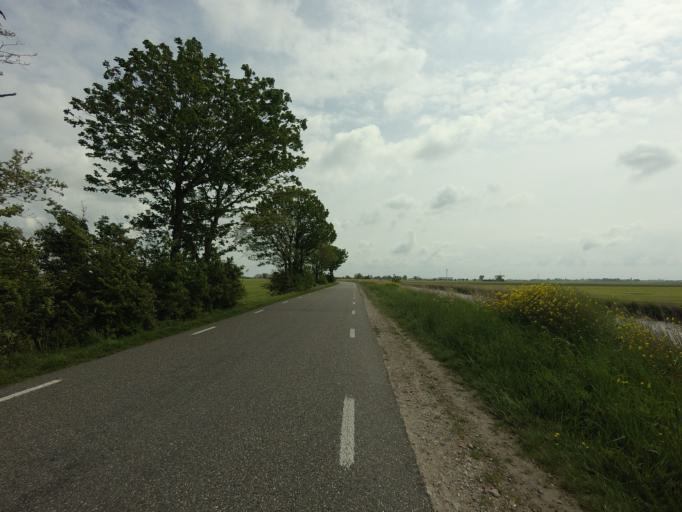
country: NL
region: Friesland
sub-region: Sudwest Fryslan
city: Bolsward
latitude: 53.1062
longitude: 5.5072
